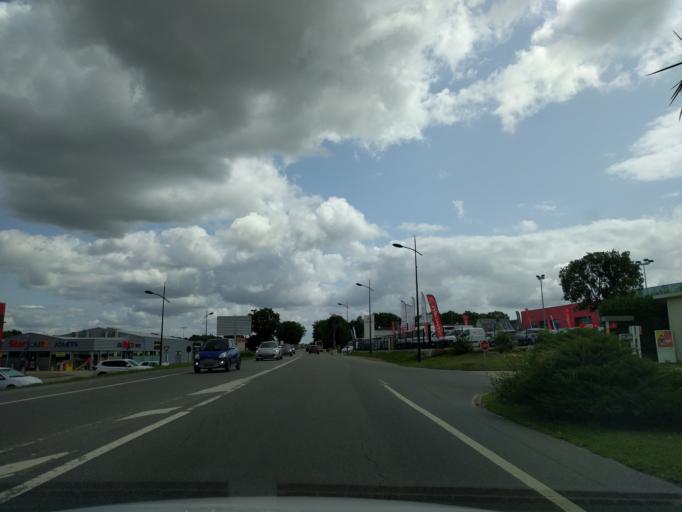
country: FR
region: Brittany
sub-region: Departement du Morbihan
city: Vannes
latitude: 47.6502
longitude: -2.7219
